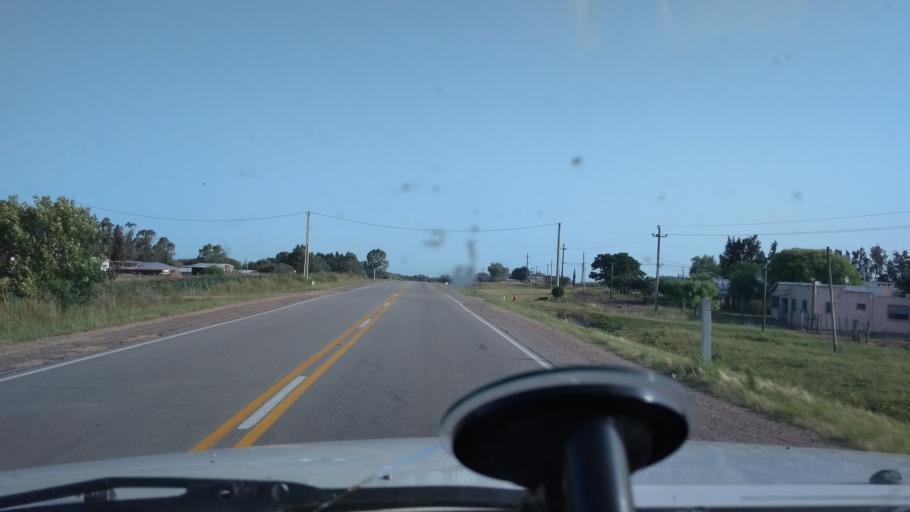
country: UY
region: Canelones
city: Santa Rosa
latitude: -34.5475
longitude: -56.0606
